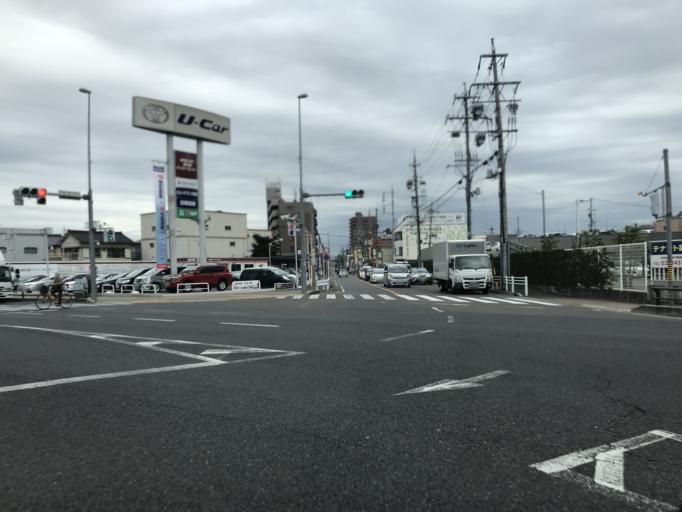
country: JP
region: Aichi
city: Nagoya-shi
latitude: 35.1916
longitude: 136.8784
